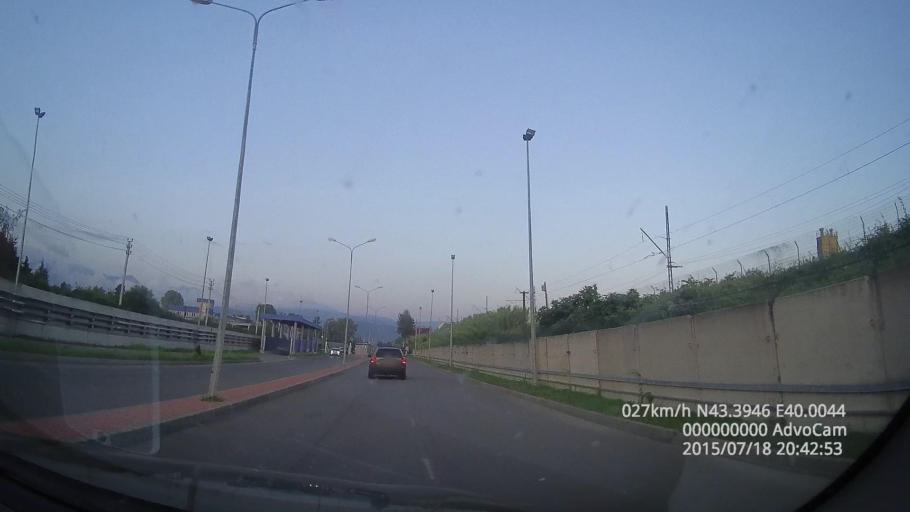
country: GE
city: Gantiadi
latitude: 43.3942
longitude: 40.0072
